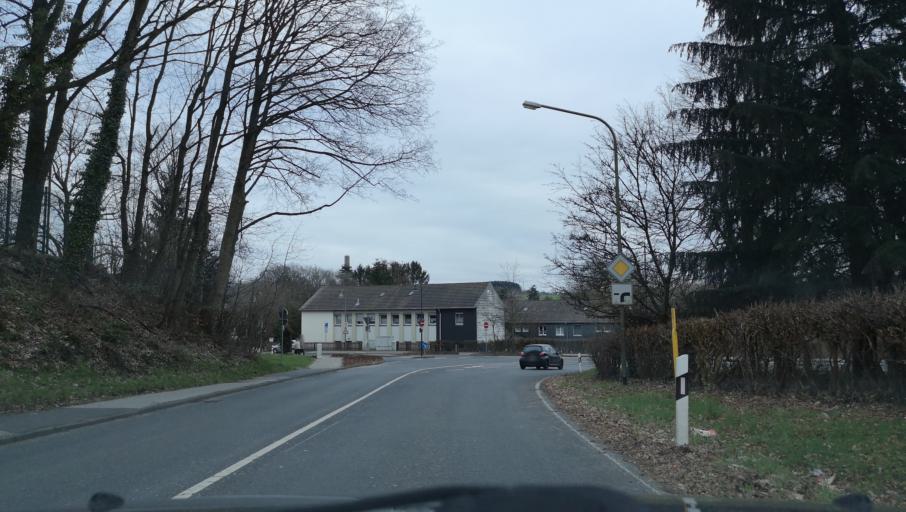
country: DE
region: North Rhine-Westphalia
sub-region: Regierungsbezirk Dusseldorf
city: Remscheid
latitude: 51.2071
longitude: 7.2308
